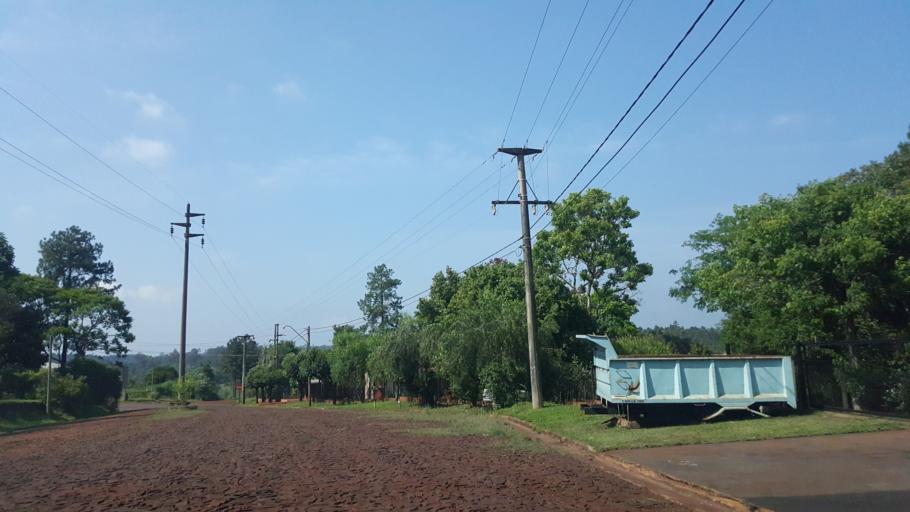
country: AR
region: Misiones
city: Capiovi
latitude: -26.9343
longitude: -55.0653
